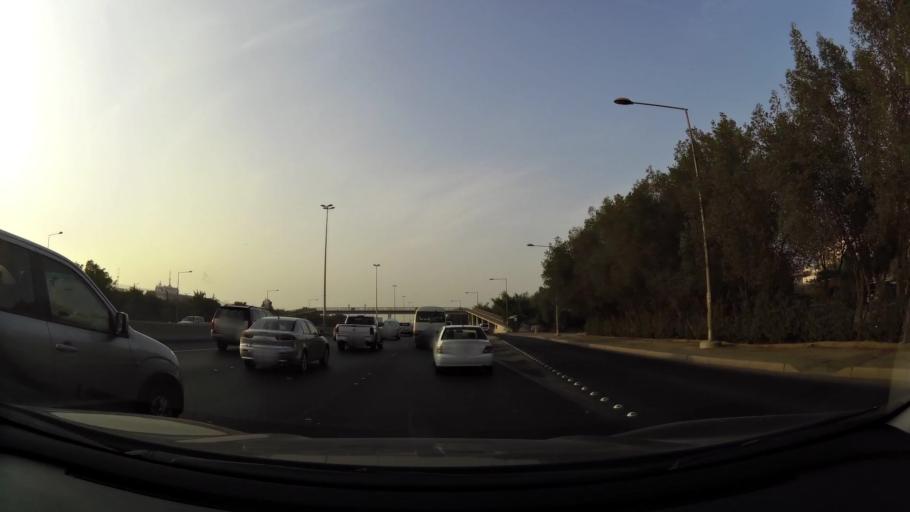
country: KW
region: Muhafazat Hawalli
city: Salwa
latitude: 29.2775
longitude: 48.0802
